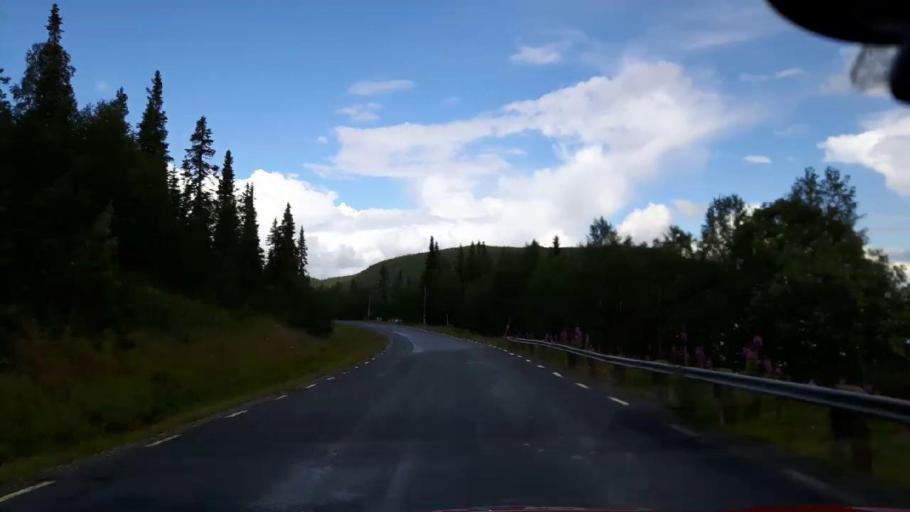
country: SE
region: Vaesterbotten
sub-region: Vilhelmina Kommun
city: Sjoberg
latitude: 65.0187
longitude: 15.1672
